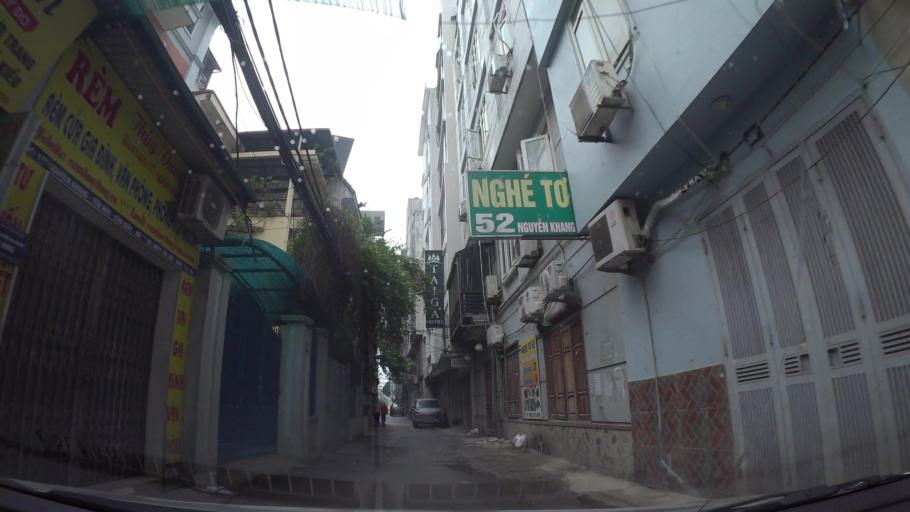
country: VN
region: Ha Noi
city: Cau Giay
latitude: 21.0213
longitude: 105.8001
